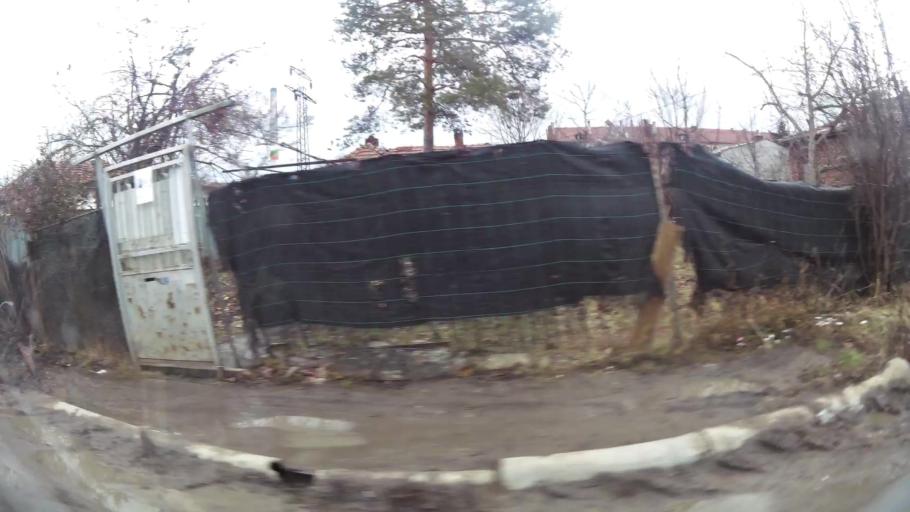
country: BG
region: Sofia-Capital
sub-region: Stolichna Obshtina
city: Sofia
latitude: 42.7231
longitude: 23.2801
